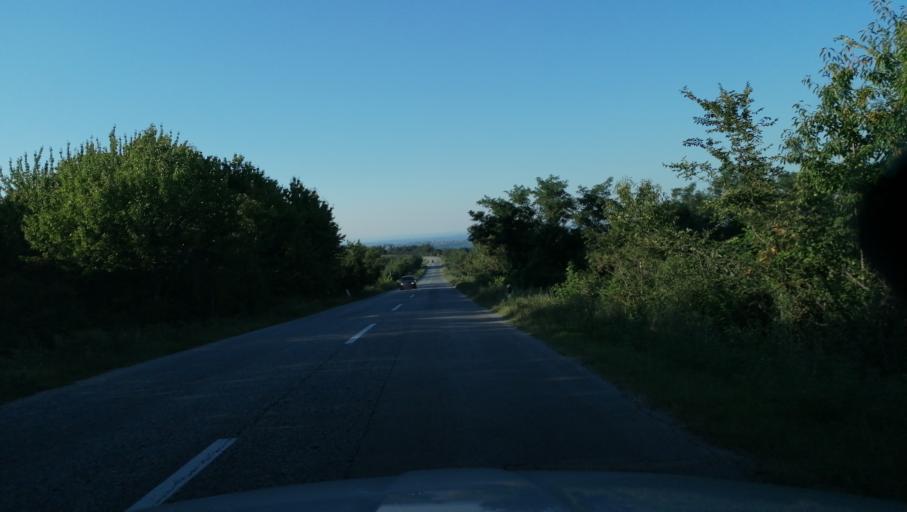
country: RS
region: Central Serbia
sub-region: Sumadijski Okrug
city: Topola
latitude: 44.1486
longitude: 20.7412
